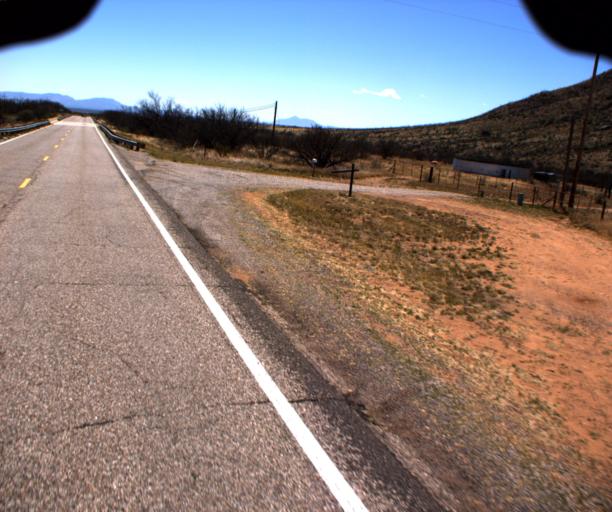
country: US
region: Arizona
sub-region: Cochise County
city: Huachuca City
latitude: 31.7001
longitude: -110.4286
